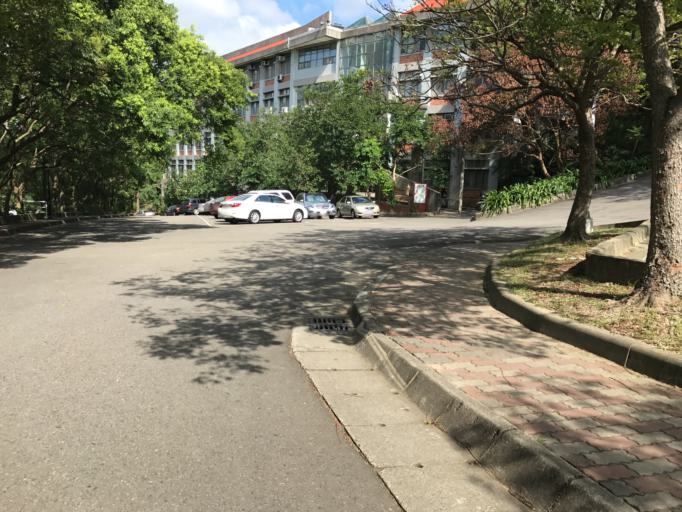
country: TW
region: Taiwan
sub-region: Hsinchu
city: Hsinchu
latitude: 24.7600
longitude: 120.9547
